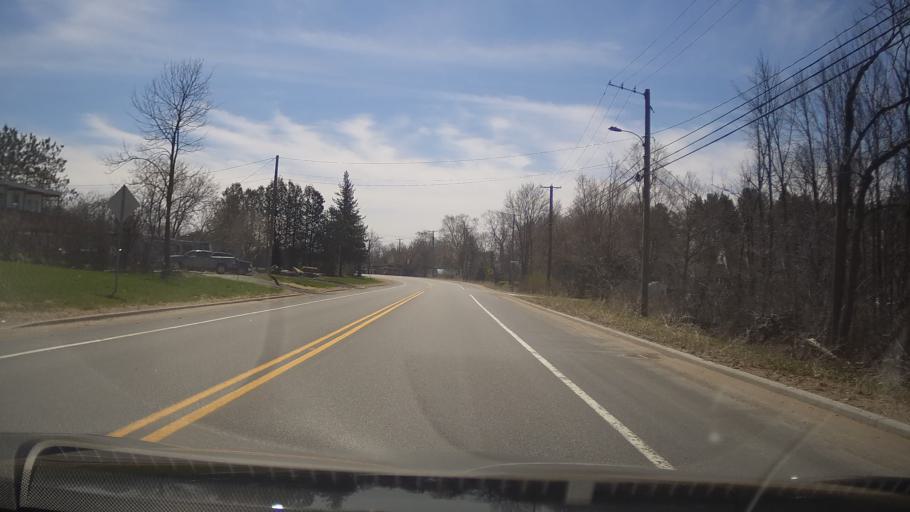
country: CA
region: Ontario
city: Bells Corners
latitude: 45.4446
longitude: -75.9198
